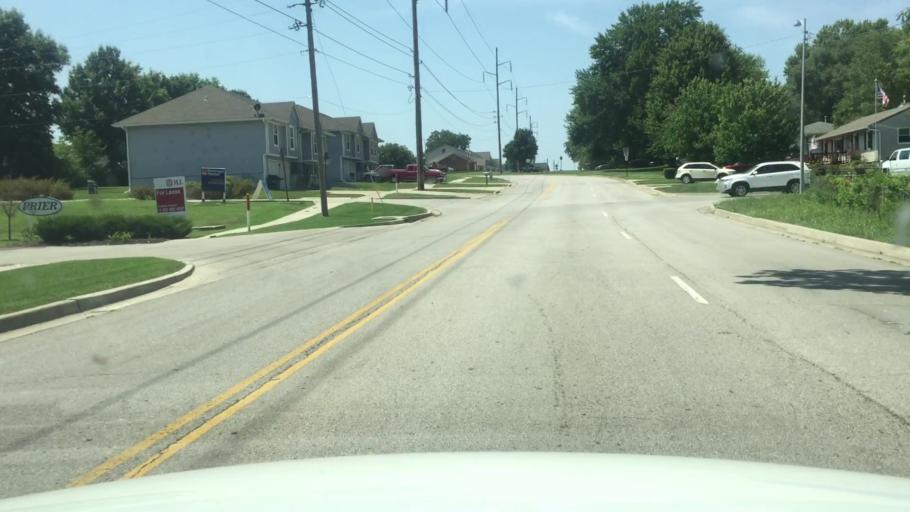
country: US
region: Missouri
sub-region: Jackson County
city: Grandview
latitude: 38.8732
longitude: -94.5408
